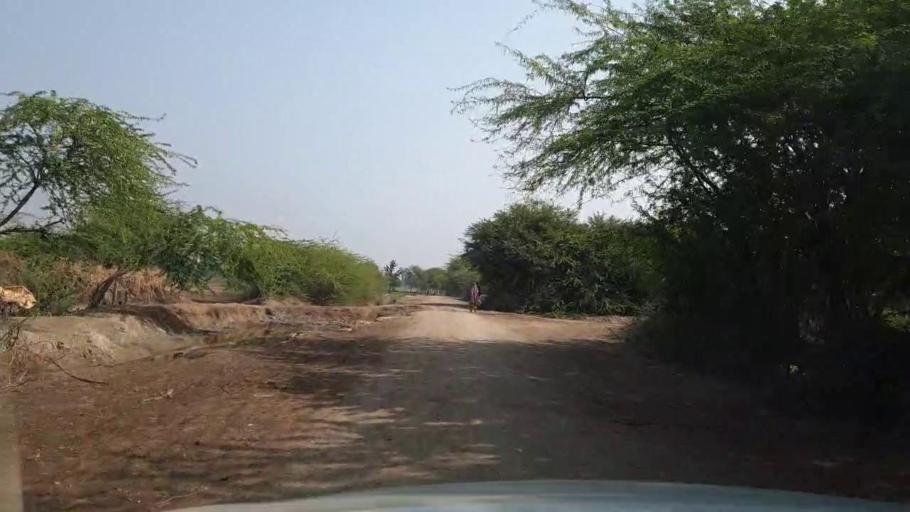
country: PK
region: Sindh
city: Umarkot
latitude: 25.4412
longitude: 69.7250
